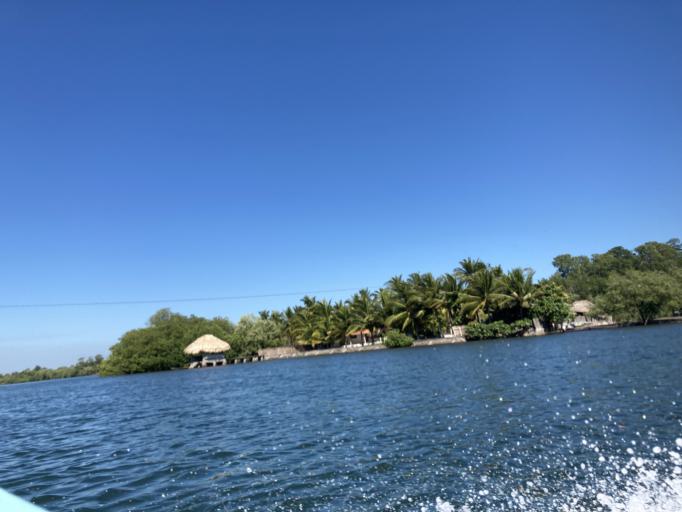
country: GT
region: Jutiapa
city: Pasaco
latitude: 13.8048
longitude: -90.2684
